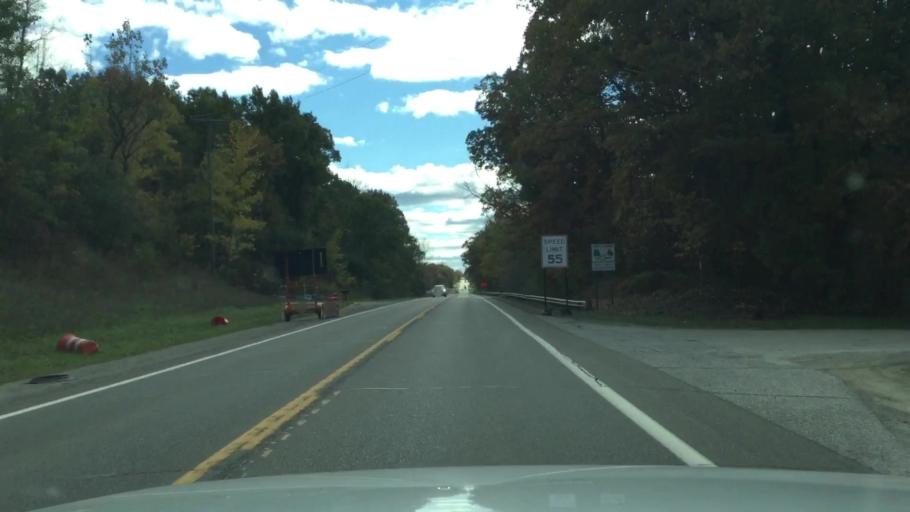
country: US
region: Michigan
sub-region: Lapeer County
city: Barnes Lake-Millers Lake
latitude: 43.1749
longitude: -83.3121
